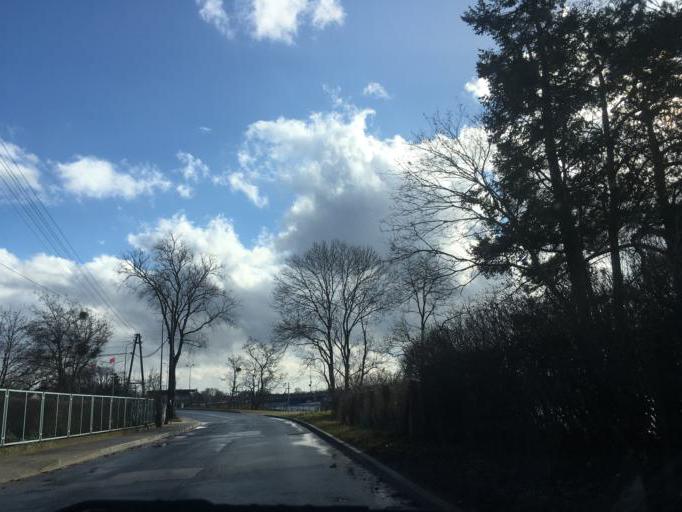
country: PL
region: Pomeranian Voivodeship
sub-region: Powiat gdanski
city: Cedry Wielkie
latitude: 54.3445
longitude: 18.8237
